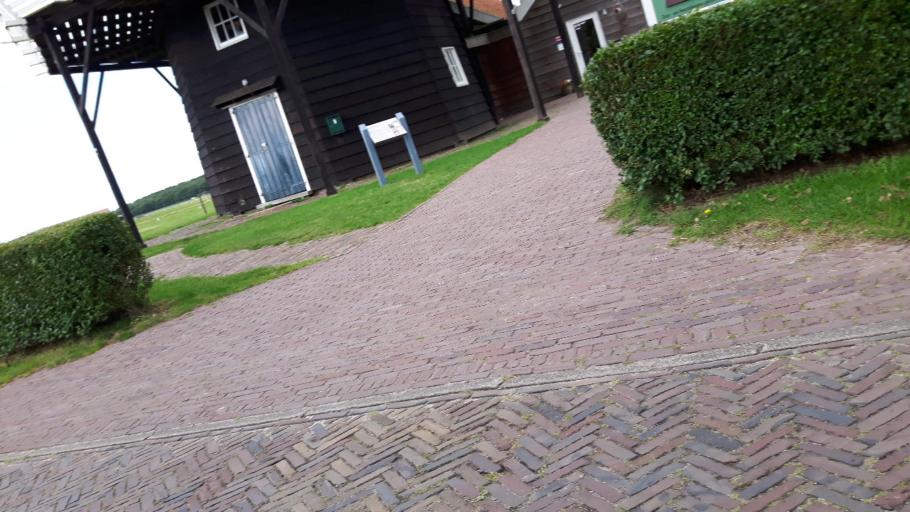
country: NL
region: Friesland
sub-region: Gemeente Ameland
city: Hollum
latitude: 53.4401
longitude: 5.6338
